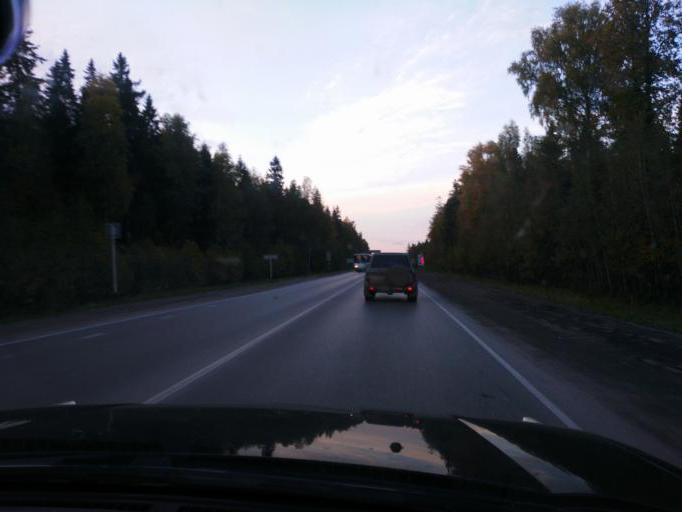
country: RU
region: Perm
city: Polazna
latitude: 58.1407
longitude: 56.4204
